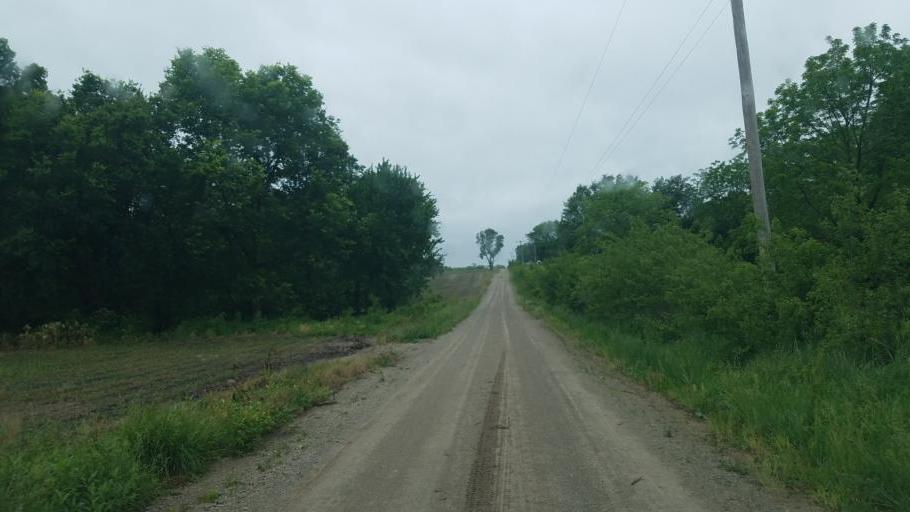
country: US
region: Missouri
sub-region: Carroll County
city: Carrollton
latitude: 39.4708
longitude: -93.4682
